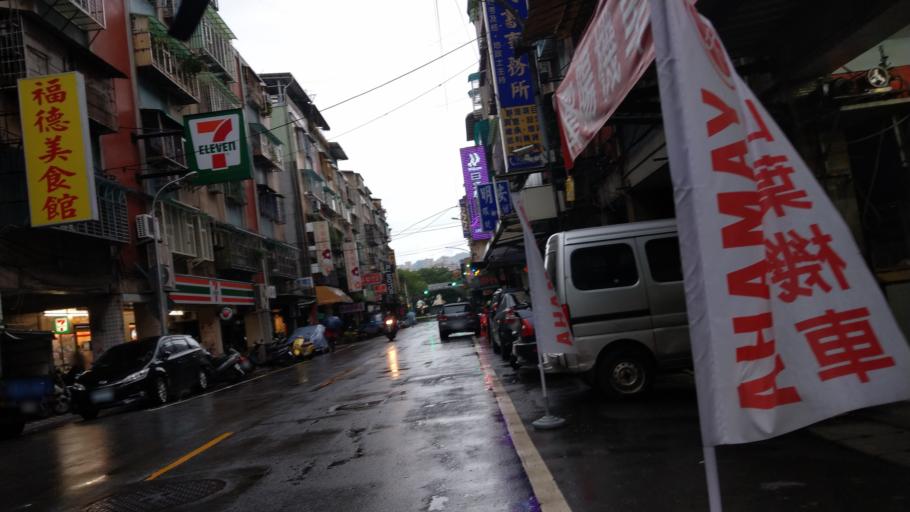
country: TW
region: Taipei
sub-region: Taipei
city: Banqiao
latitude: 24.9939
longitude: 121.4644
